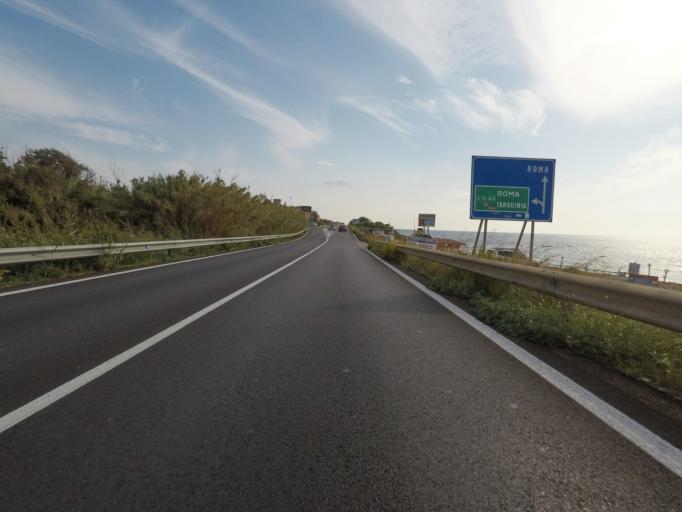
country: IT
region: Latium
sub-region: Citta metropolitana di Roma Capitale
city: Civitavecchia
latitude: 42.0564
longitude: 11.8197
